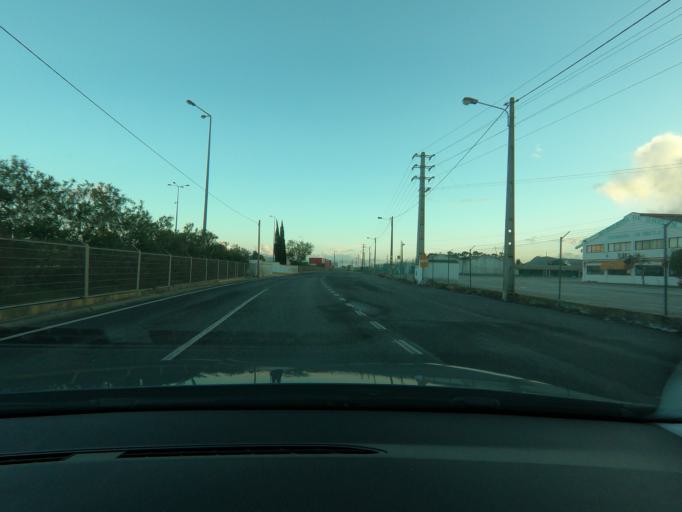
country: PT
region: Lisbon
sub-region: Vila Franca de Xira
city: Castanheira do Ribatejo
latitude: 38.9951
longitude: -8.9631
